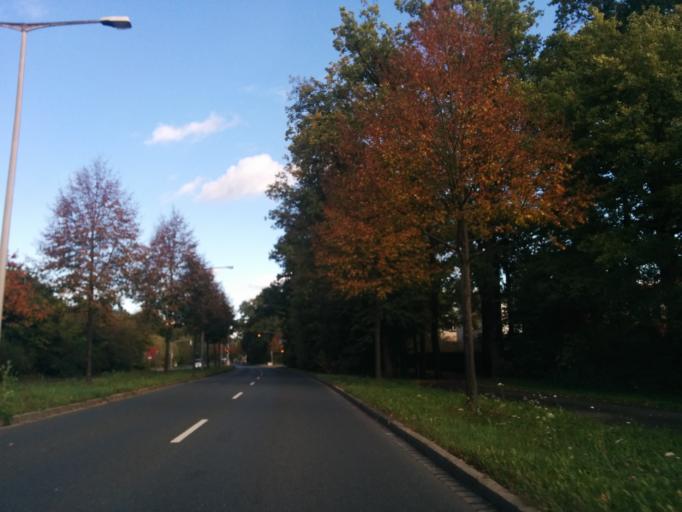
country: DE
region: Bavaria
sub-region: Regierungsbezirk Mittelfranken
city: Nuernberg
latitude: 49.4843
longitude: 11.1205
